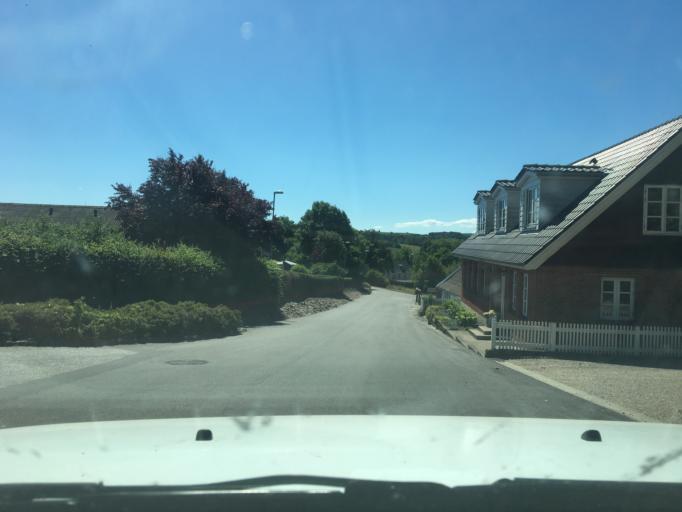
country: DK
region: Central Jutland
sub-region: Syddjurs Kommune
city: Hornslet
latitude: 56.3313
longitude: 10.3768
